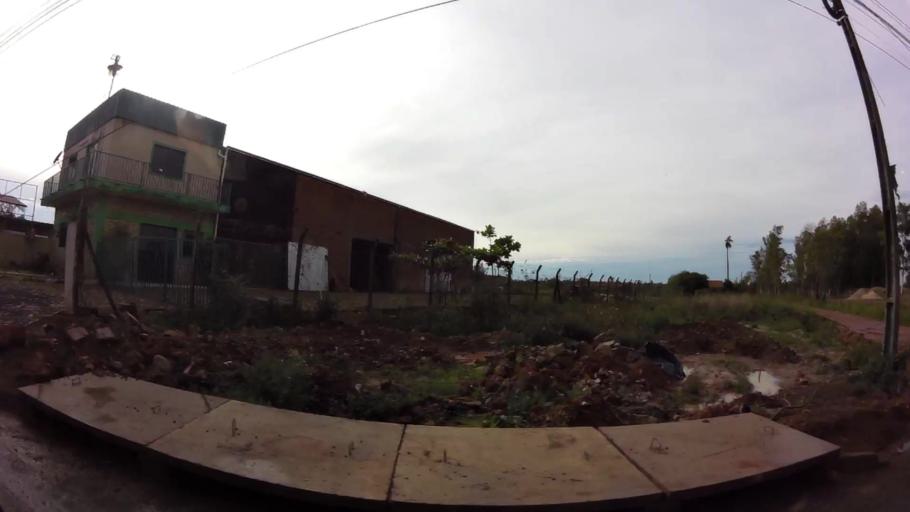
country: PY
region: Central
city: Limpio
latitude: -25.1859
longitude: -57.4949
